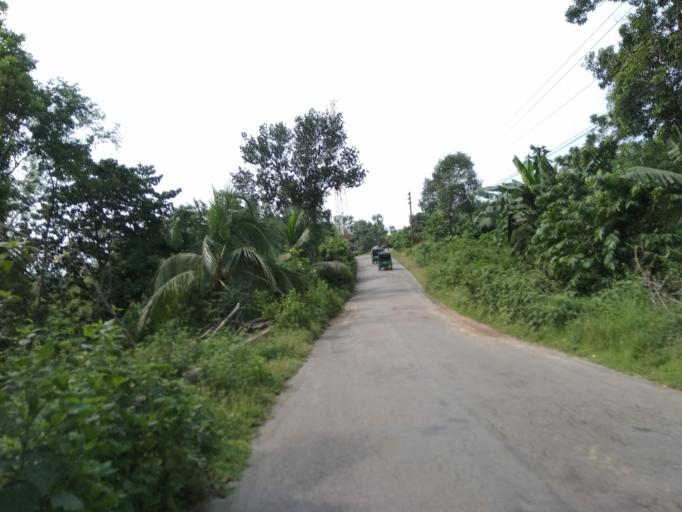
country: BD
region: Chittagong
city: Khagrachhari
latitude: 22.9976
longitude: 92.0115
